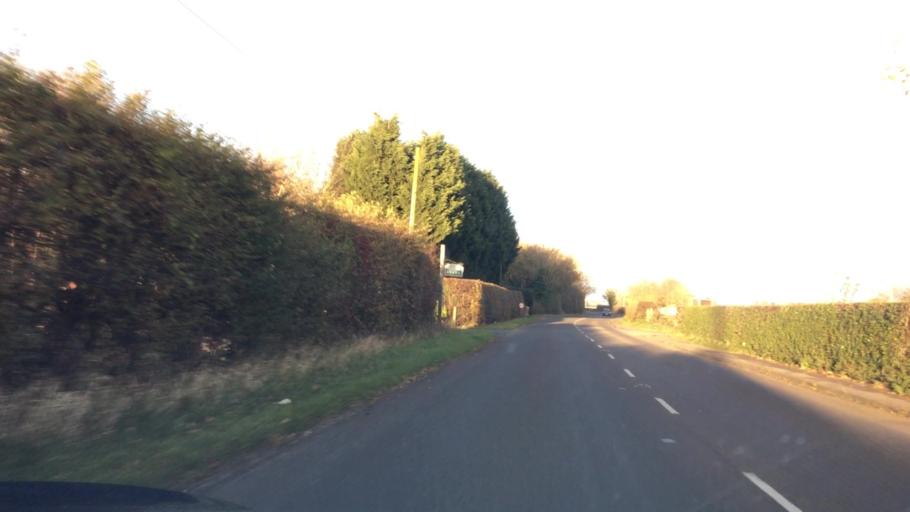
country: GB
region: England
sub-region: Derbyshire
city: Melbourne
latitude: 52.8211
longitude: -1.4428
